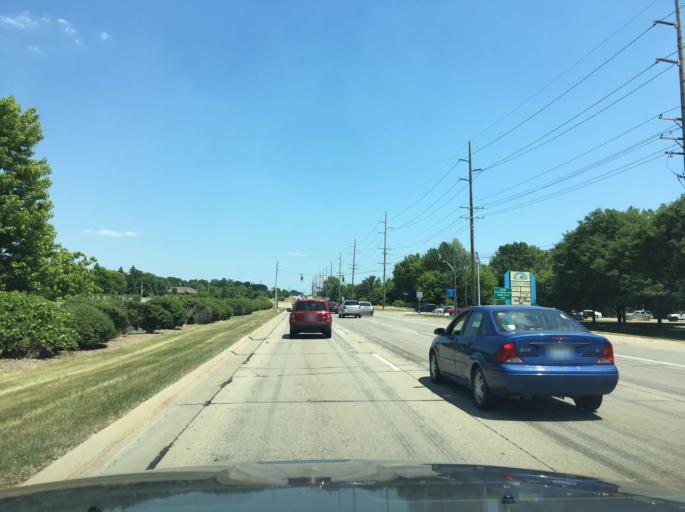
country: US
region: Michigan
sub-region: Macomb County
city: Mount Clemens
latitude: 42.6285
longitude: -82.8883
